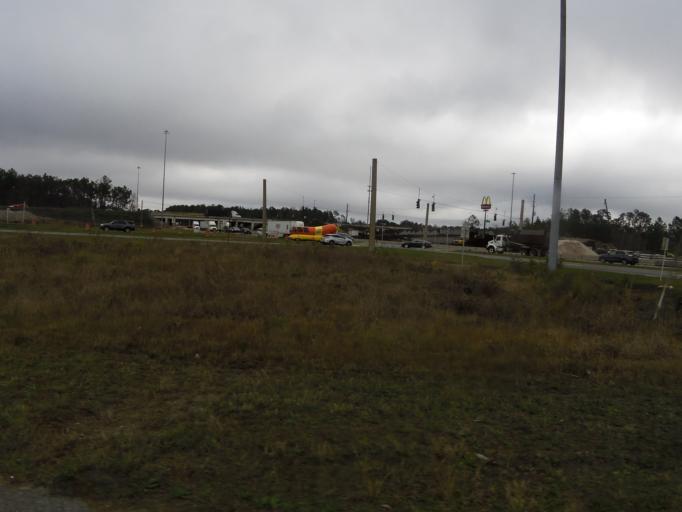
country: US
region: Florida
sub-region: Duval County
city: Baldwin
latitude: 30.2867
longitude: -81.9834
